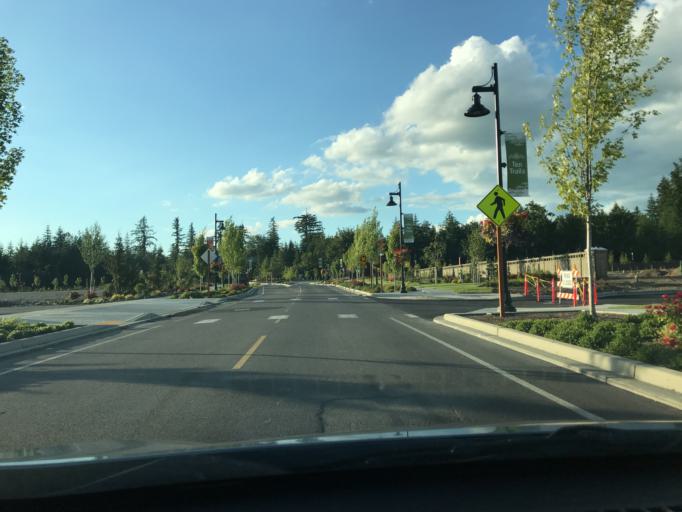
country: US
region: Washington
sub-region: King County
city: Black Diamond
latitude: 47.3101
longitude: -122.0297
